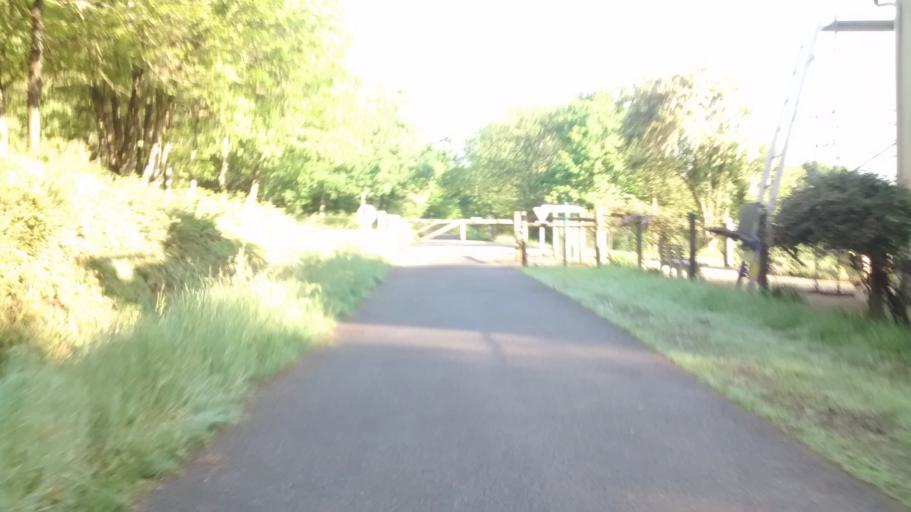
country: FR
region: Brittany
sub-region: Departement du Morbihan
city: Pleucadeuc
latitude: 47.7711
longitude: -2.3958
